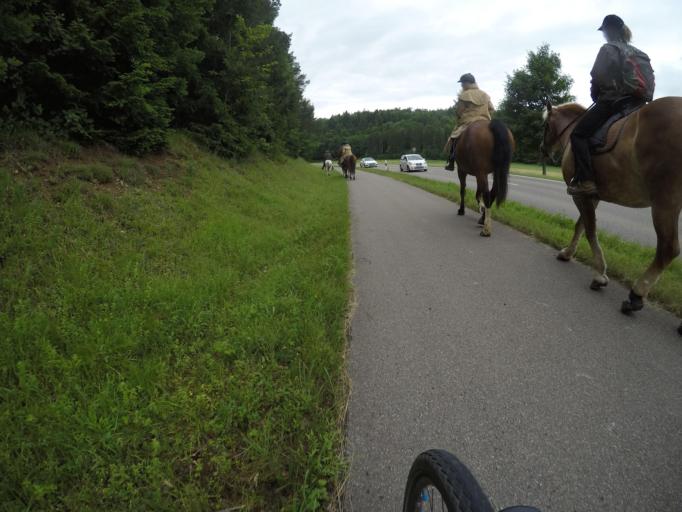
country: DE
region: Baden-Wuerttemberg
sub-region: Regierungsbezirk Stuttgart
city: Aidlingen
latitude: 48.6637
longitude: 8.8761
